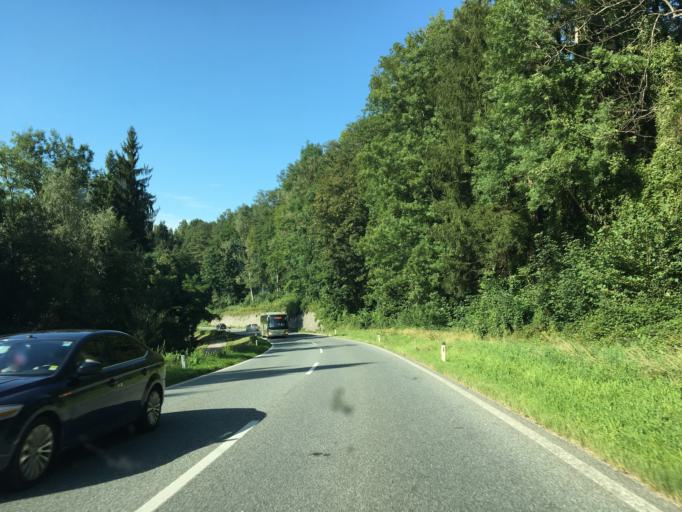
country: AT
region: Carinthia
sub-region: Politischer Bezirk Volkermarkt
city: Voelkermarkt
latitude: 46.6418
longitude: 14.6311
